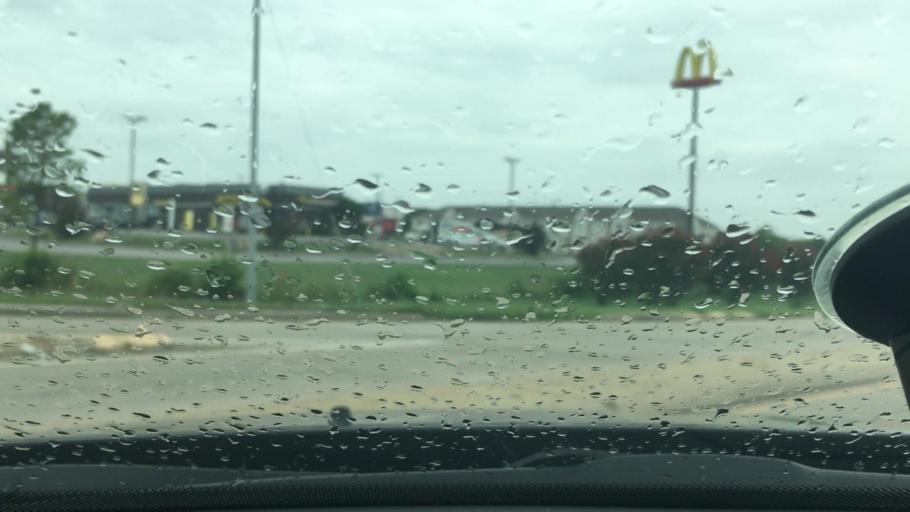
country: US
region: Oklahoma
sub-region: Carter County
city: Ardmore
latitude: 34.1893
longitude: -97.1684
